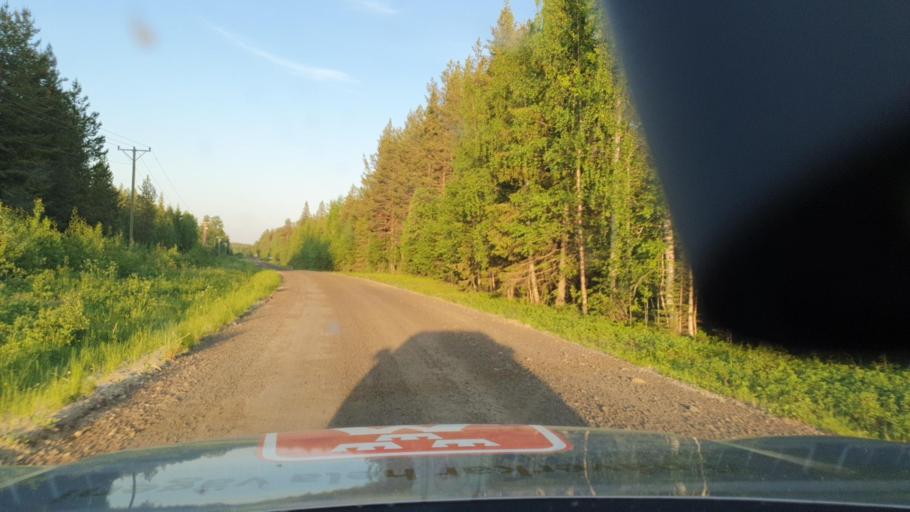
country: SE
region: Norrbotten
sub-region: Bodens Kommun
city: Boden
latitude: 66.0834
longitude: 21.6211
